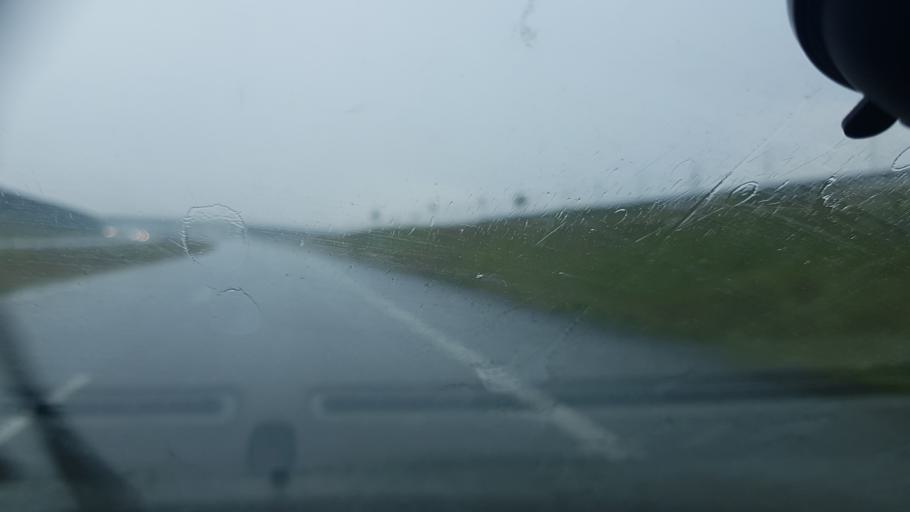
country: PL
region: Warmian-Masurian Voivodeship
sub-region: Powiat nidzicki
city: Nidzica
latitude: 53.4342
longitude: 20.3402
